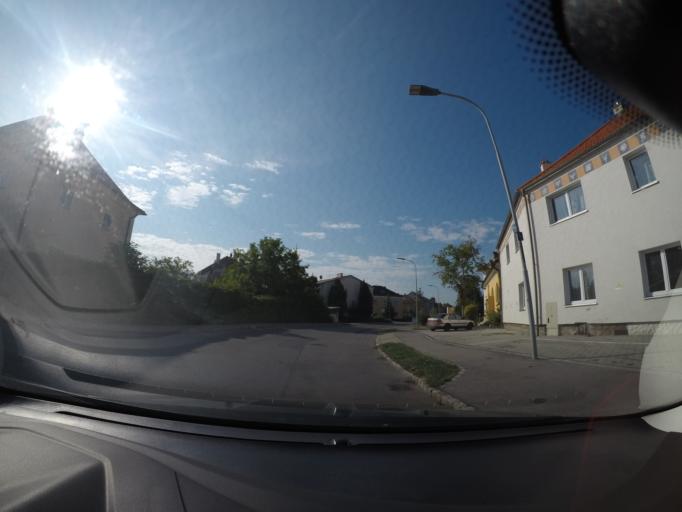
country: AT
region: Lower Austria
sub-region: Politischer Bezirk Baden
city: Tattendorf
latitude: 47.9274
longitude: 16.3022
